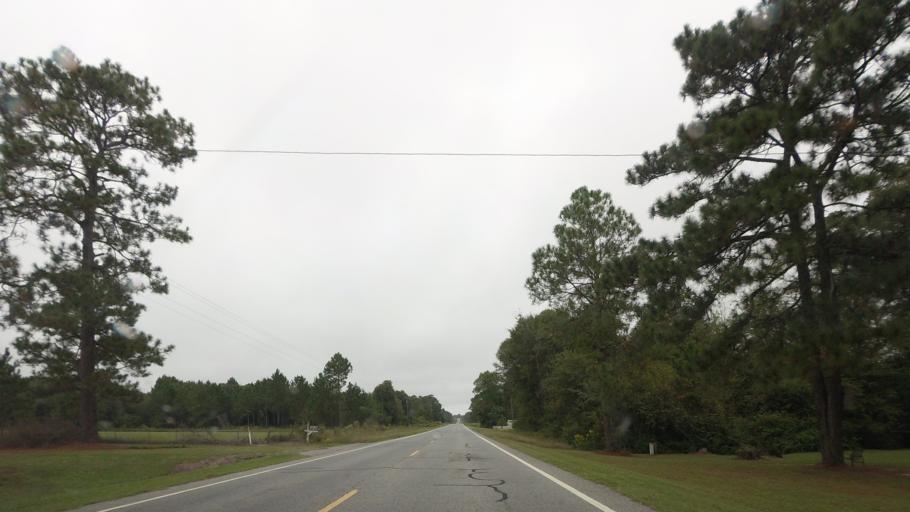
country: US
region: Georgia
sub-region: Irwin County
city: Ocilla
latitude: 31.4909
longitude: -83.2384
